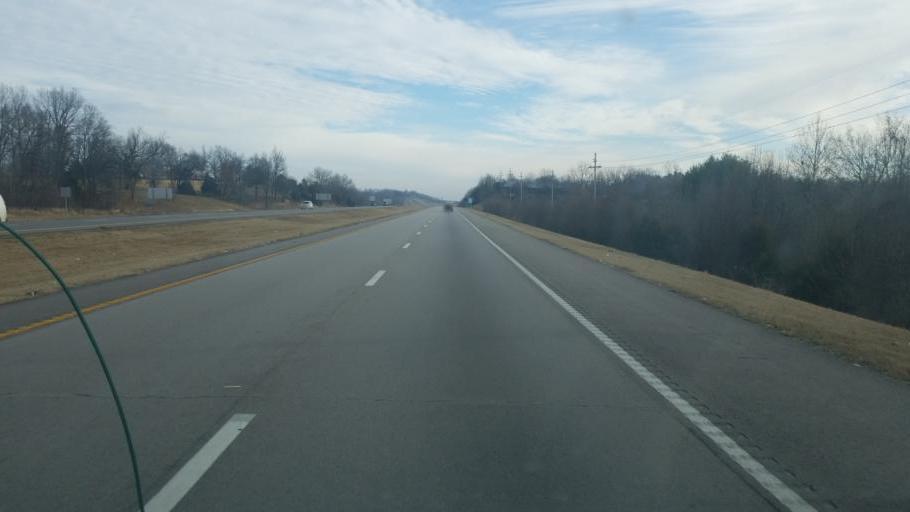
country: US
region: Missouri
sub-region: Stoddard County
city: Dexter
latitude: 36.8113
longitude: -89.9617
